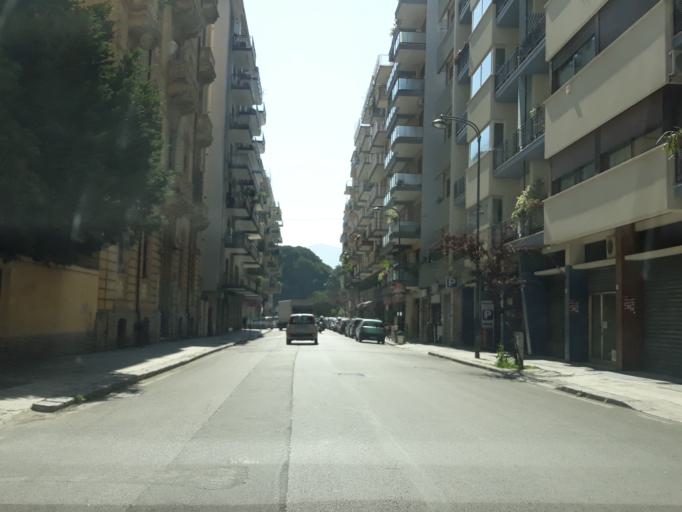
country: IT
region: Sicily
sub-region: Palermo
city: Palermo
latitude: 38.1356
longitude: 13.3504
